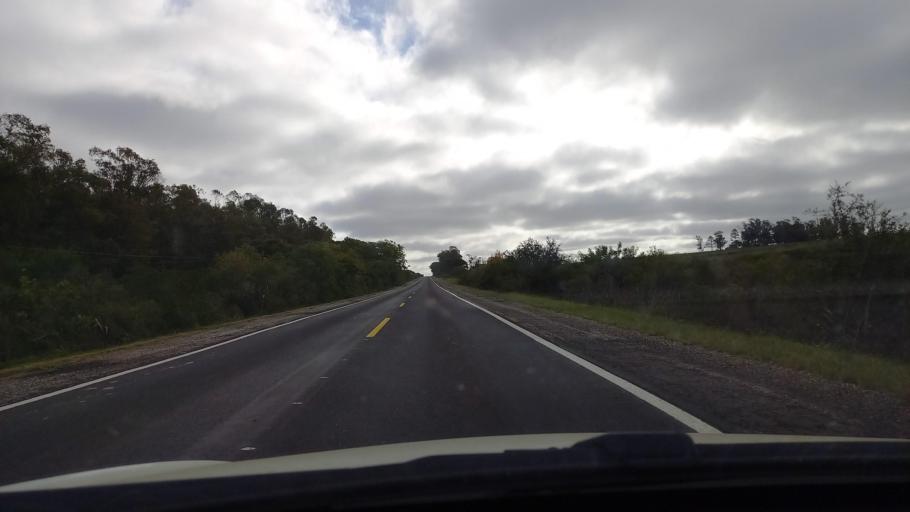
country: BR
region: Rio Grande do Sul
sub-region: Dom Pedrito
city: Dom Pedrito
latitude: -30.9120
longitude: -54.8063
